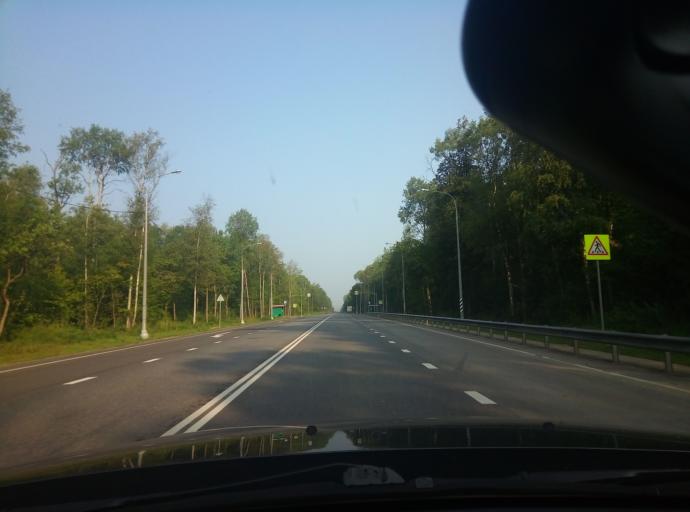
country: RU
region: Kaluga
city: Kaluga
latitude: 54.4419
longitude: 36.3265
